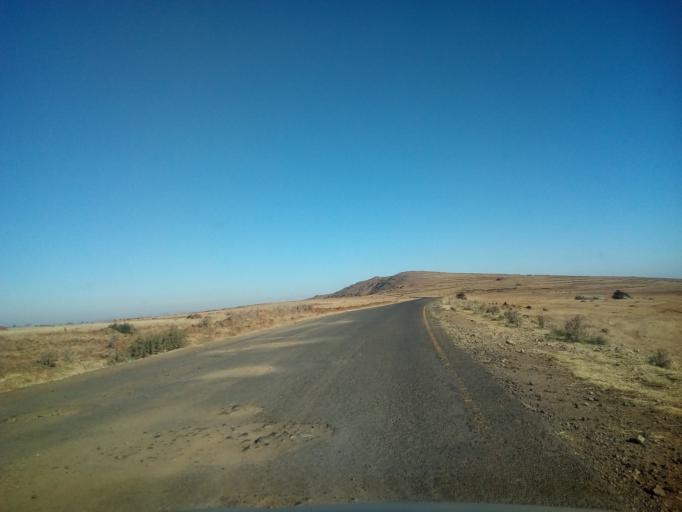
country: LS
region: Berea
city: Teyateyaneng
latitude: -29.2541
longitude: 27.7808
